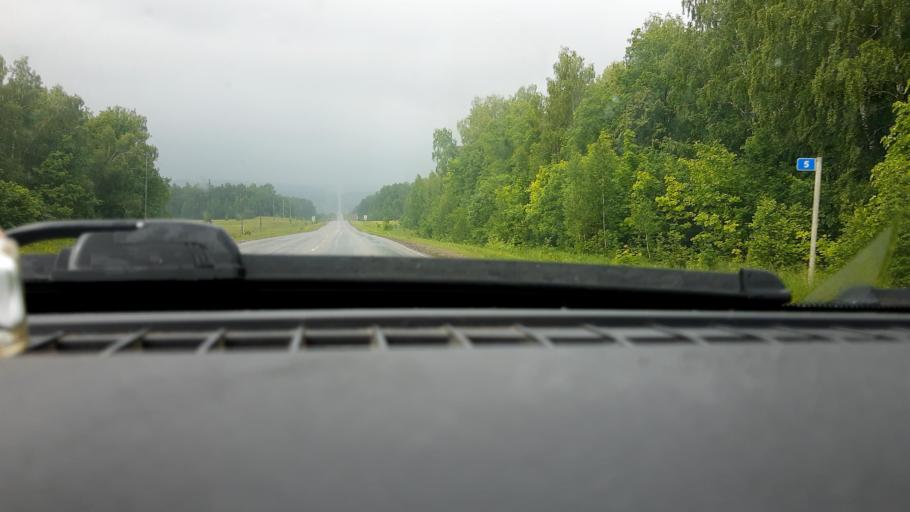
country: RU
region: Bashkortostan
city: Belebey
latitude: 54.1707
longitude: 54.0838
